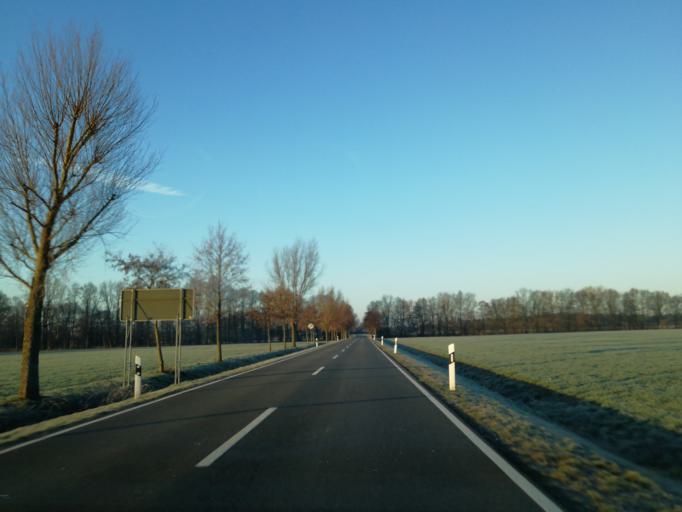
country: DE
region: Brandenburg
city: Finsterwalde
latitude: 51.6690
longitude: 13.7184
